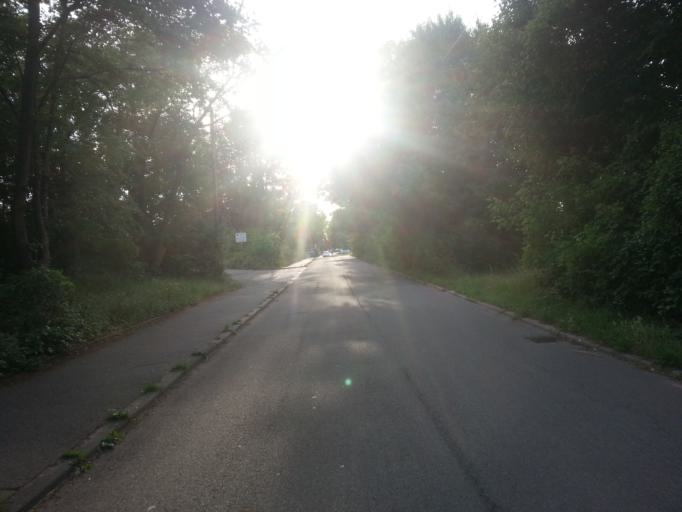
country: DE
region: Rheinland-Pfalz
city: Altrip
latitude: 49.4476
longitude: 8.4914
